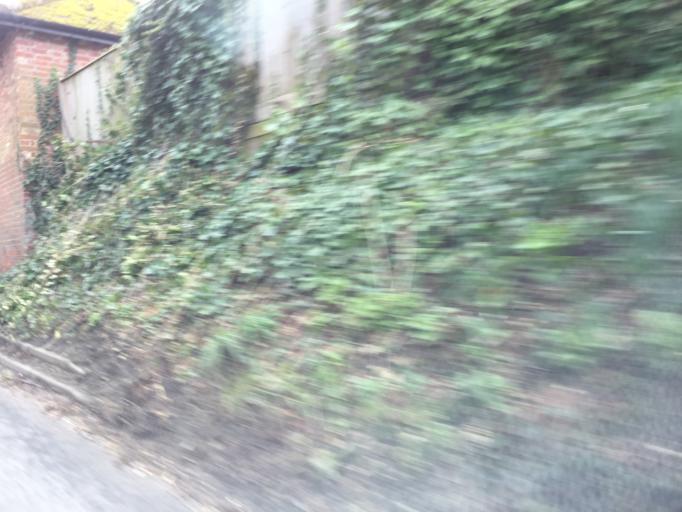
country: GB
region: England
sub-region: Oxfordshire
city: Goring
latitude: 51.5291
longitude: -1.1511
